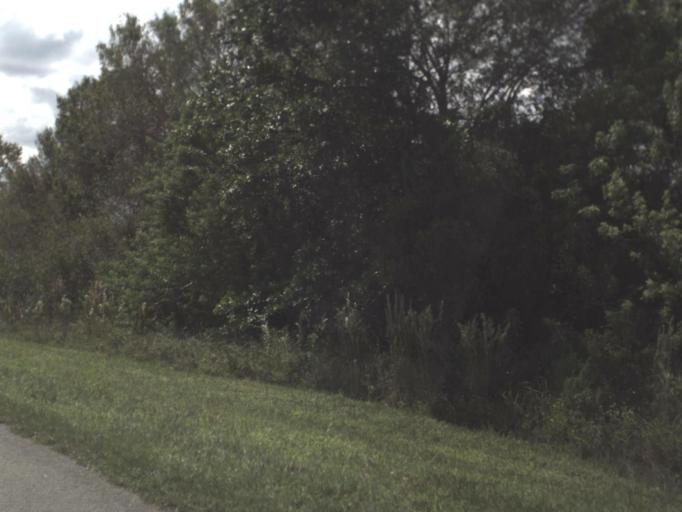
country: US
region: Florida
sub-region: Collier County
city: Immokalee
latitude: 26.2868
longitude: -81.3425
